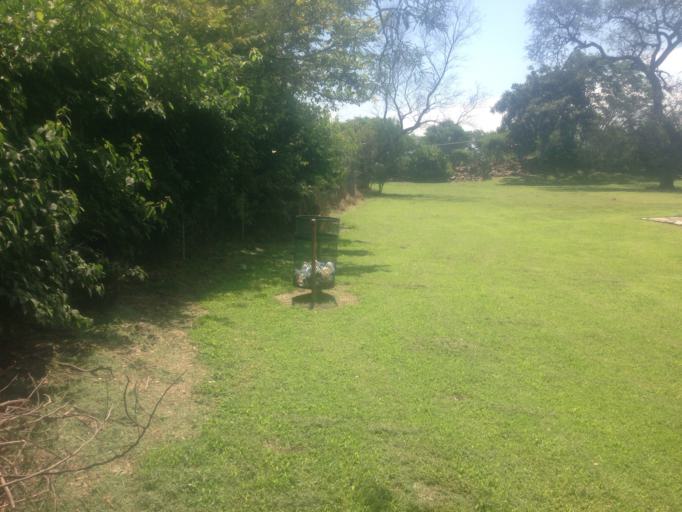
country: MX
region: Nayarit
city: Ixtlan del Rio
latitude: 21.0403
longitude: -104.3443
